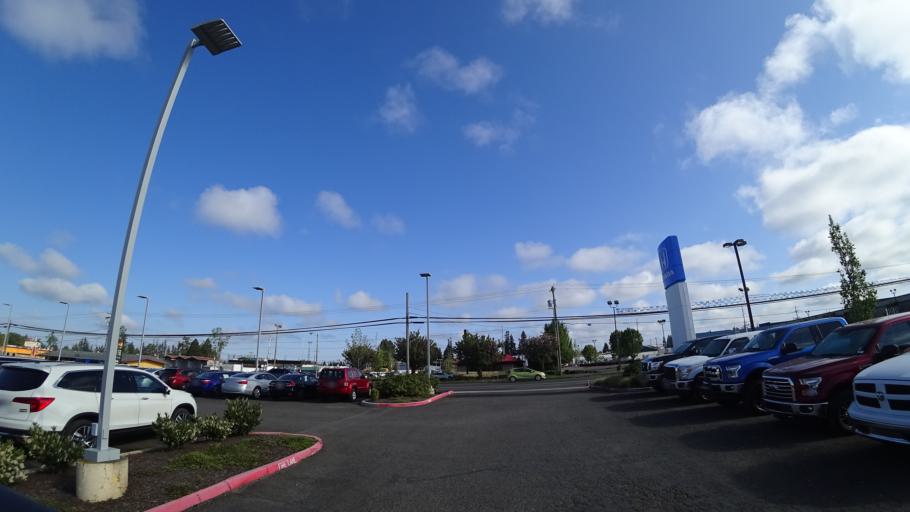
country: US
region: Oregon
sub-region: Washington County
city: Hillsboro
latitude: 45.5186
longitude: -122.9982
